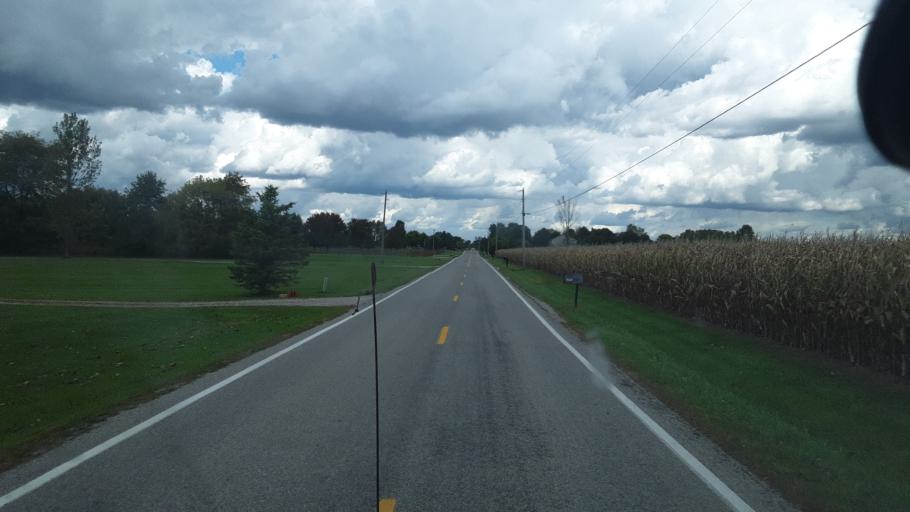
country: US
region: Ohio
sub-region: Knox County
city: Centerburg
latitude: 40.2527
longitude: -82.7526
